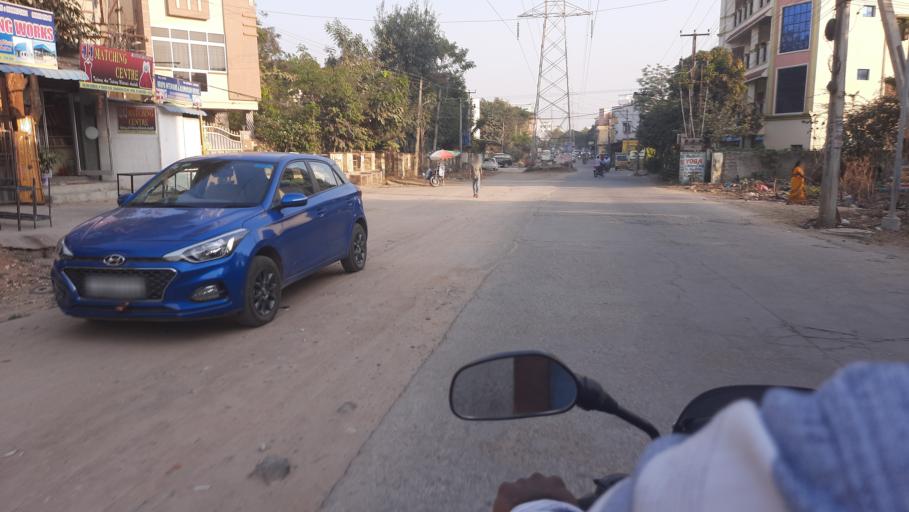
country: IN
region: Telangana
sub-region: Rangareddi
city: Secunderabad
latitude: 17.4987
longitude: 78.5413
